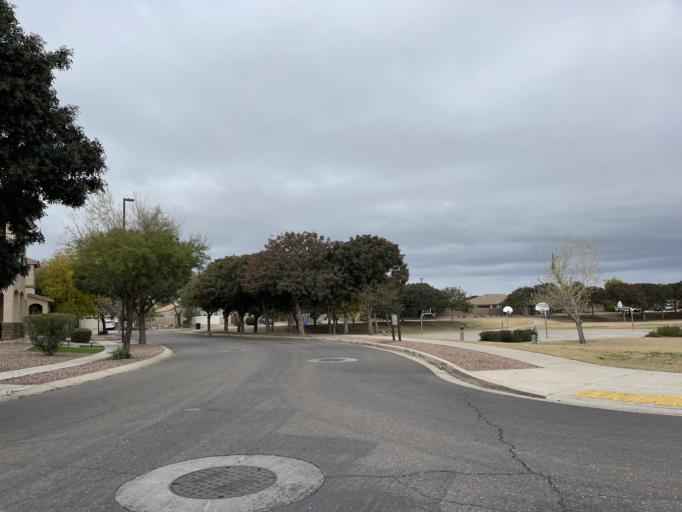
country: US
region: Arizona
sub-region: Maricopa County
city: Queen Creek
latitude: 33.2794
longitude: -111.7011
